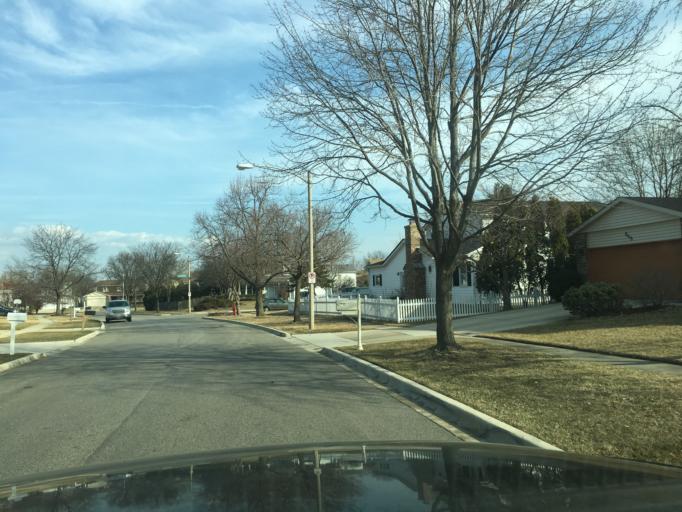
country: US
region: Illinois
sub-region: Cook County
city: Schaumburg
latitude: 42.0418
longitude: -88.1065
